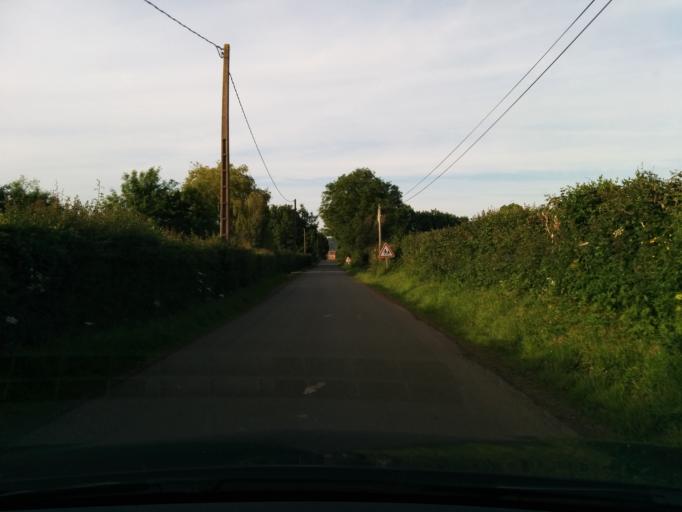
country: FR
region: Haute-Normandie
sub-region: Departement de la Seine-Maritime
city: Neufchatel-en-Bray
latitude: 49.6796
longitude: 1.4864
